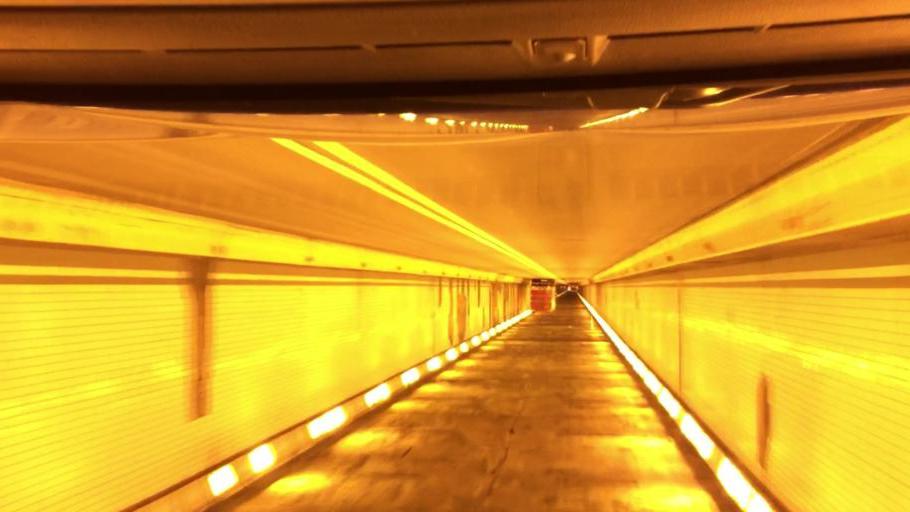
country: US
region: Pennsylvania
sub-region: Franklin County
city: Doylestown
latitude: 40.1486
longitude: -77.6597
